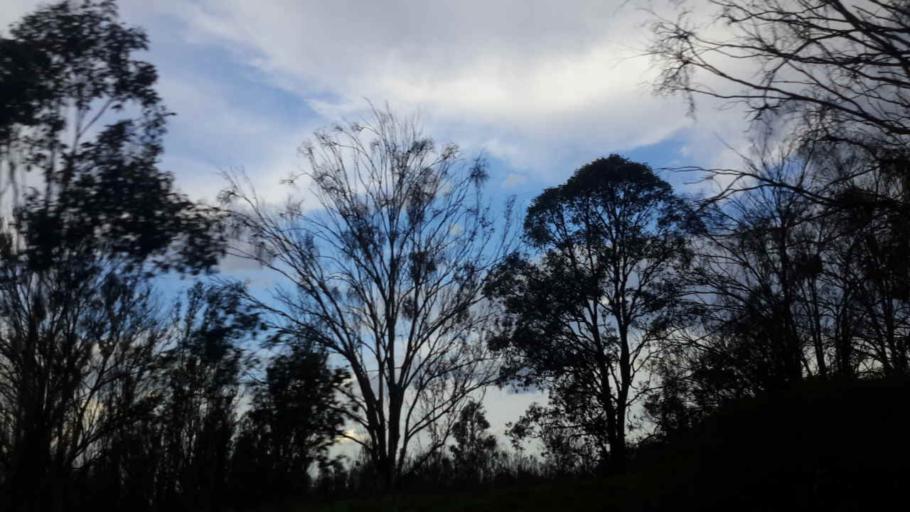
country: AU
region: New South Wales
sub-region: Penrith Municipality
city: Mulgoa
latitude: -33.8304
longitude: 150.6836
